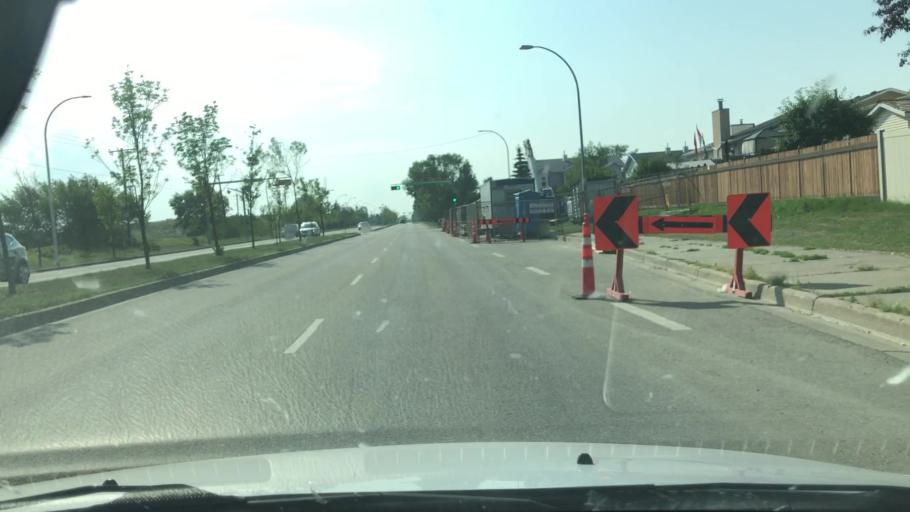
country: CA
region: Alberta
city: Edmonton
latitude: 53.6142
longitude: -113.5008
